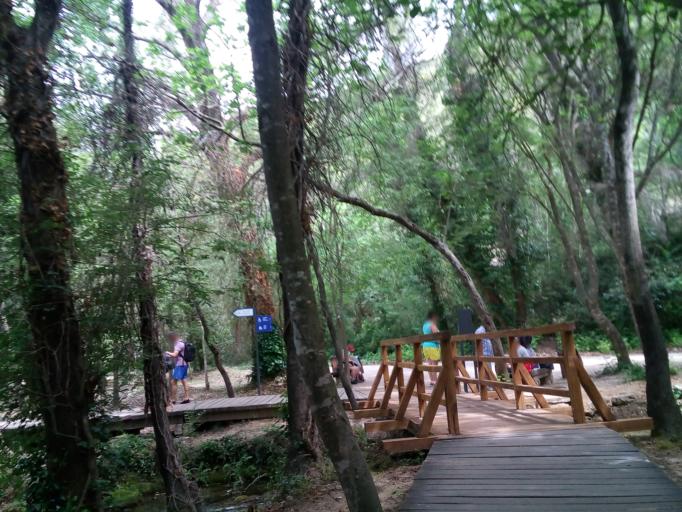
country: HR
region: Sibensko-Kniniska
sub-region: Grad Sibenik
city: Sibenik
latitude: 43.8058
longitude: 15.9668
